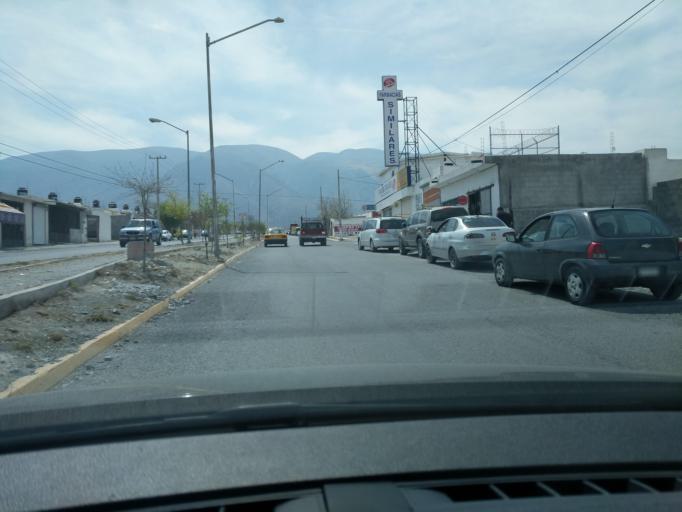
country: MX
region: Coahuila
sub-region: Arteaga
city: Arteaga
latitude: 25.4213
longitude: -100.9013
